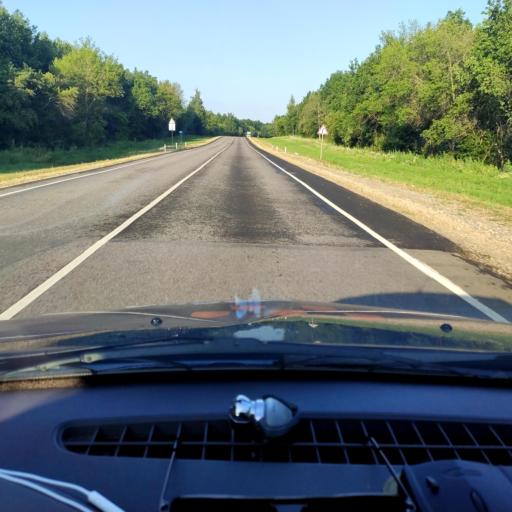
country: RU
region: Lipetsk
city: Izmalkovo
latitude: 52.4524
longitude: 37.9993
